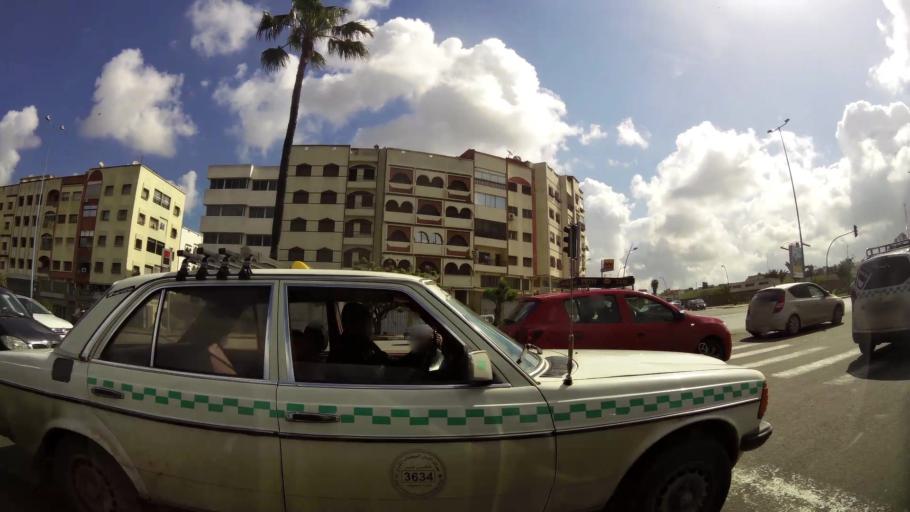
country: MA
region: Grand Casablanca
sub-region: Casablanca
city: Casablanca
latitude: 33.5512
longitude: -7.5892
